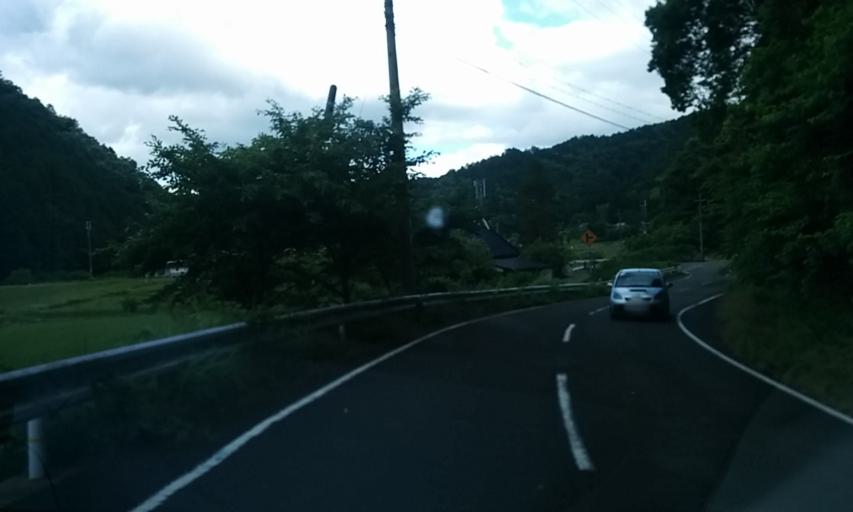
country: JP
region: Kyoto
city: Ayabe
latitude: 35.3818
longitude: 135.2138
